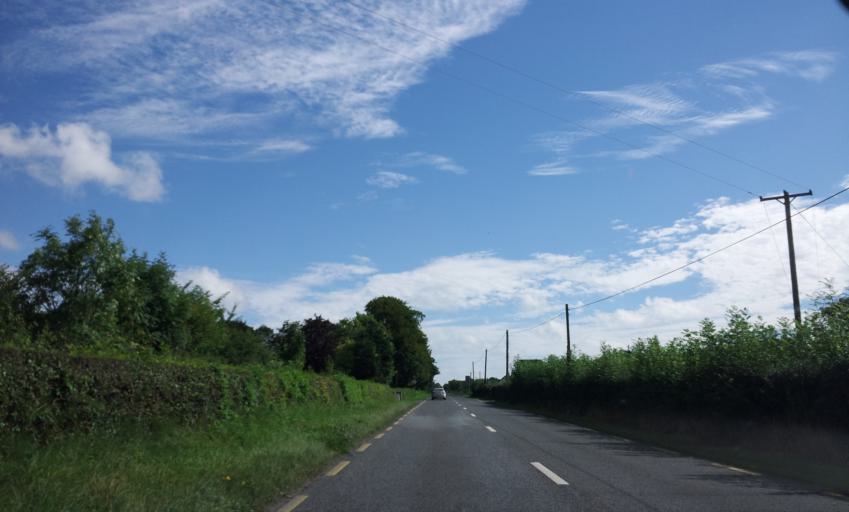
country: IE
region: Leinster
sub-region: Laois
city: Mountrath
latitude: 53.0046
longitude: -7.4652
